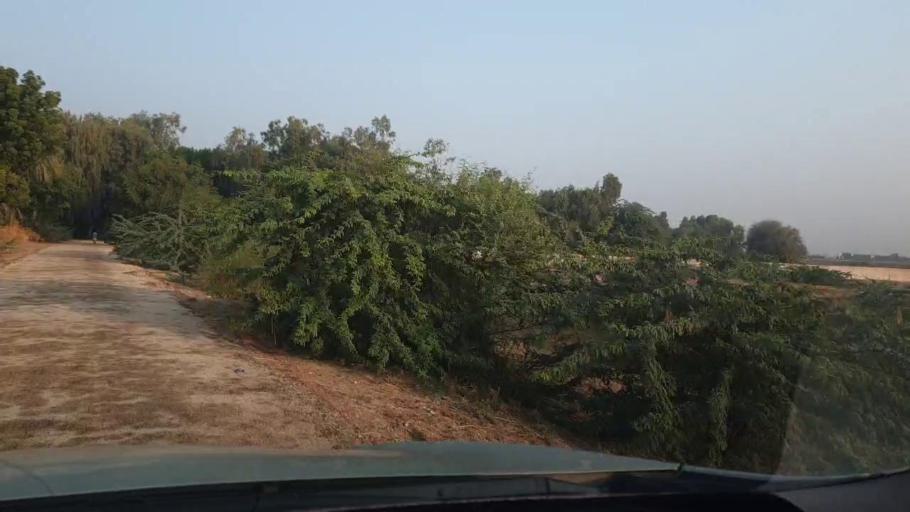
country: PK
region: Sindh
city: Sehwan
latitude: 26.3947
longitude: 67.8625
